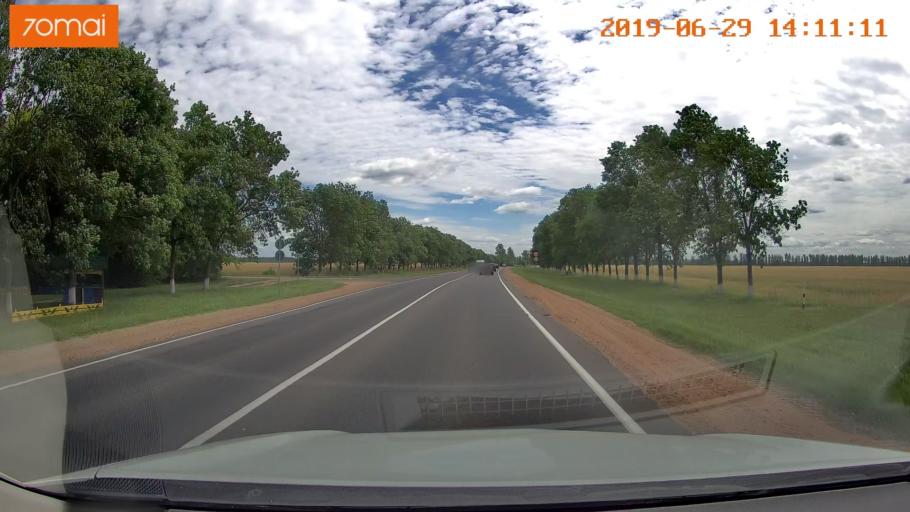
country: BY
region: Minsk
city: Salihorsk
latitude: 52.8223
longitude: 27.5010
